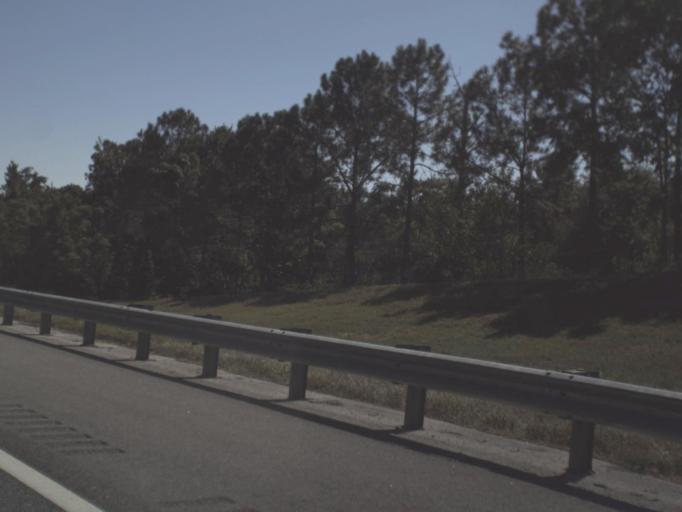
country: US
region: Florida
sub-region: Lake County
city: Montverde
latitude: 28.5605
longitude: -81.6816
